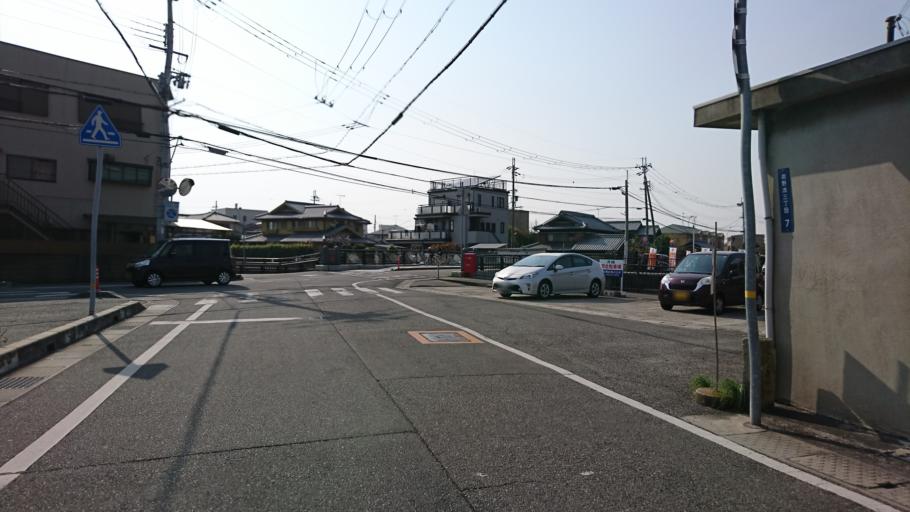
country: JP
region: Hyogo
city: Kakogawacho-honmachi
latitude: 34.7175
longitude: 134.8690
